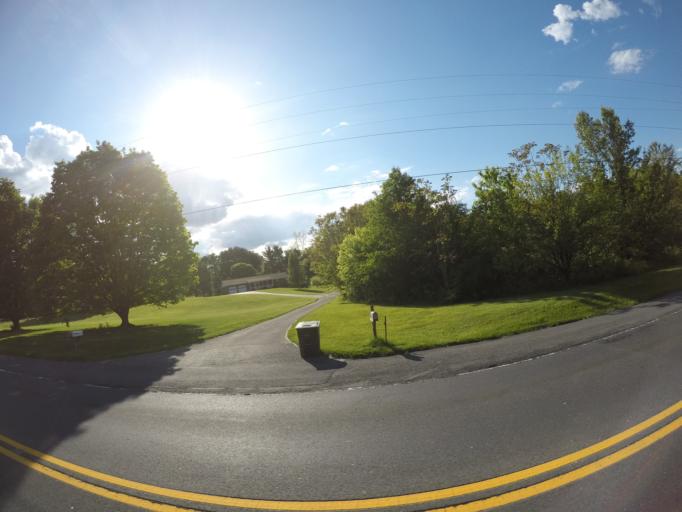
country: US
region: Maryland
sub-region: Montgomery County
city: Damascus
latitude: 39.3320
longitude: -77.1861
